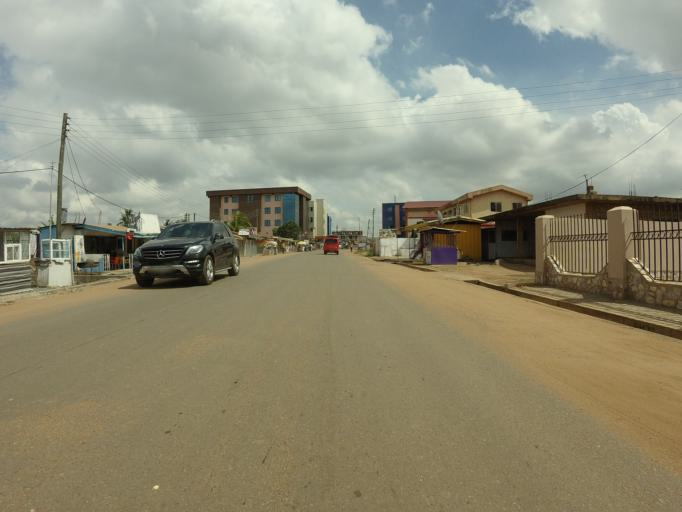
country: GH
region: Greater Accra
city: Nungua
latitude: 5.6288
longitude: -0.0927
